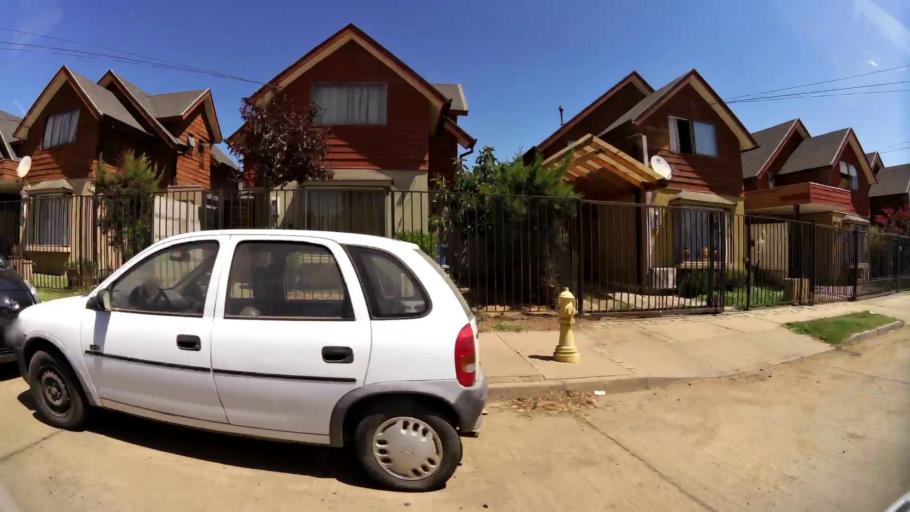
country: CL
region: Maule
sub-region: Provincia de Talca
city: Talca
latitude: -35.4250
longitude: -71.6136
